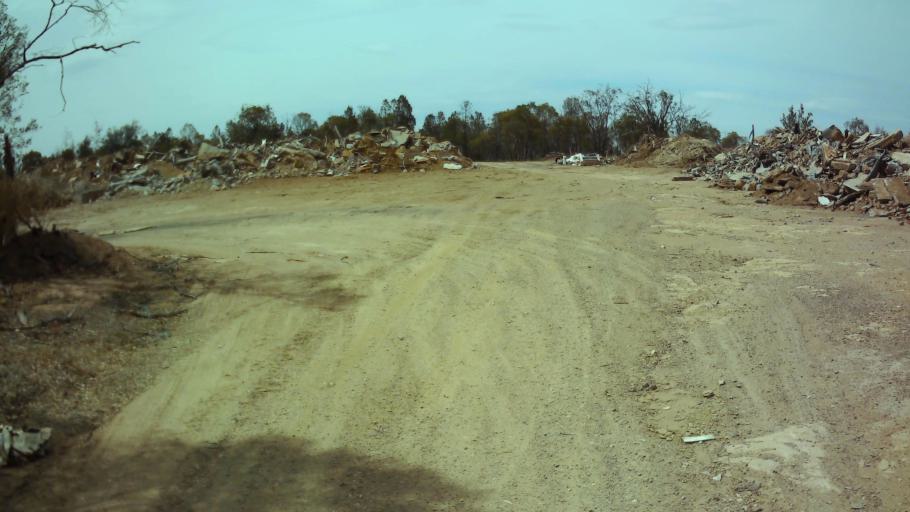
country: AU
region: New South Wales
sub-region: Weddin
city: Grenfell
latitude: -33.8678
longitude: 148.1660
